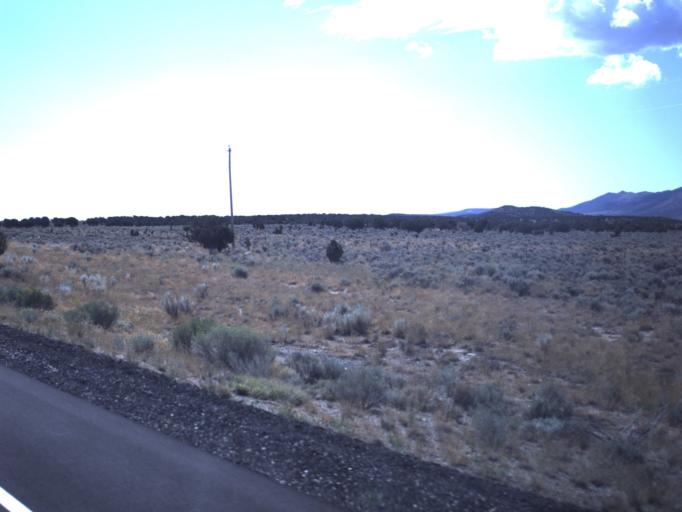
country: US
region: Utah
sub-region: Utah County
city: Eagle Mountain
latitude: 40.0706
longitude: -112.3317
